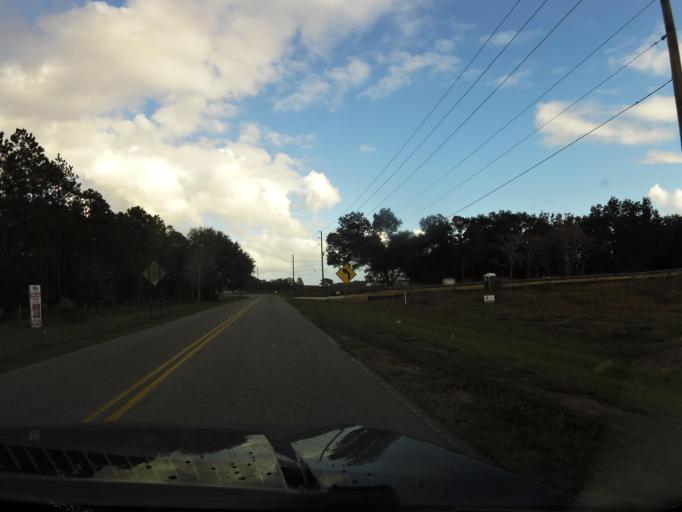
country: US
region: Florida
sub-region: Clay County
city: Asbury Lake
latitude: 30.0464
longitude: -81.7783
